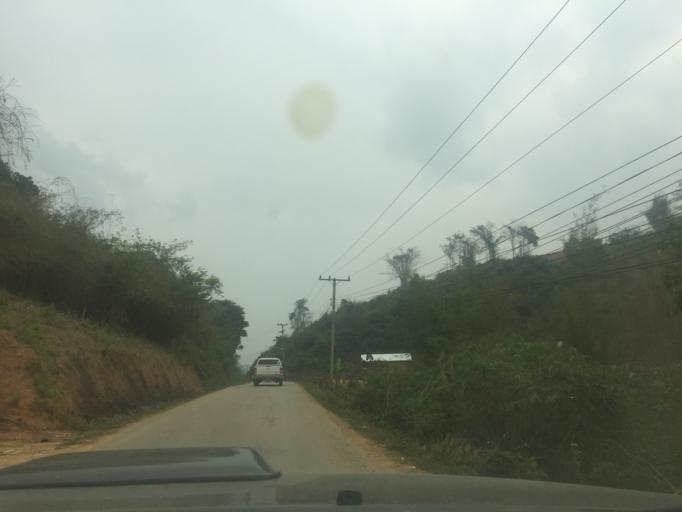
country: LA
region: Vientiane
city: Muang Sanakham
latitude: 18.4016
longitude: 101.5131
